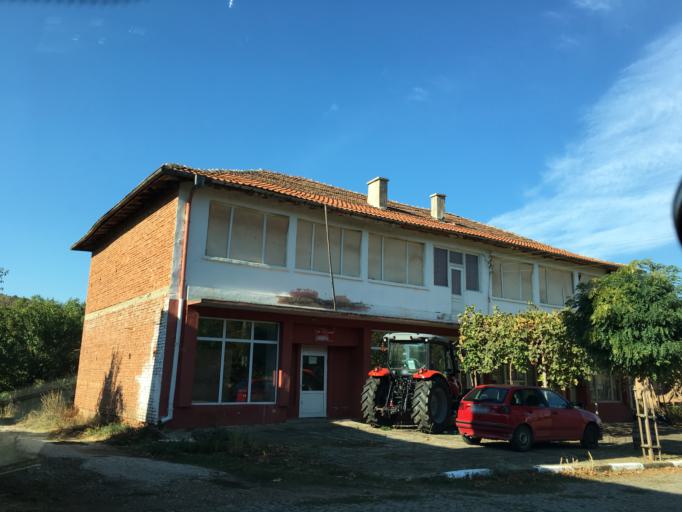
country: BG
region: Khaskovo
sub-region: Obshtina Ivaylovgrad
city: Ivaylovgrad
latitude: 41.3914
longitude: 26.1323
